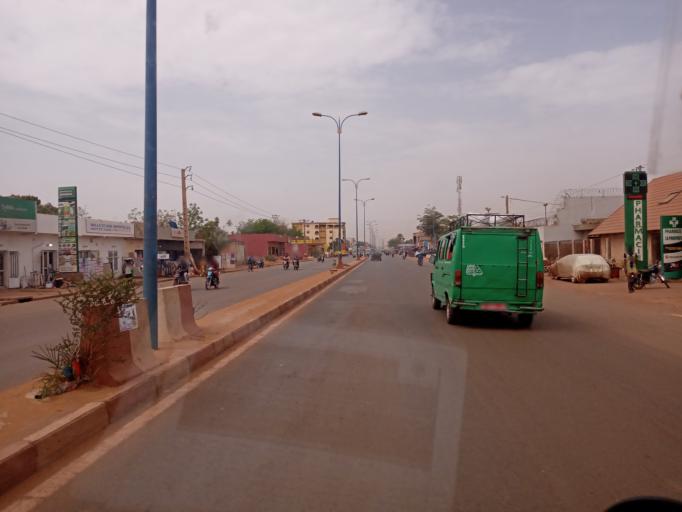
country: ML
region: Bamako
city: Bamako
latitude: 12.6046
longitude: -8.0491
